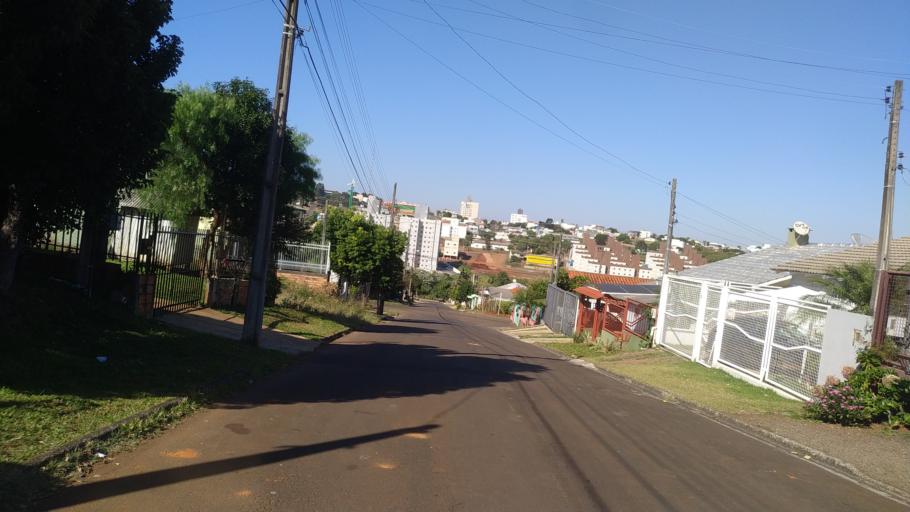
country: BR
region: Santa Catarina
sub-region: Chapeco
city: Chapeco
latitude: -27.0833
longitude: -52.6016
